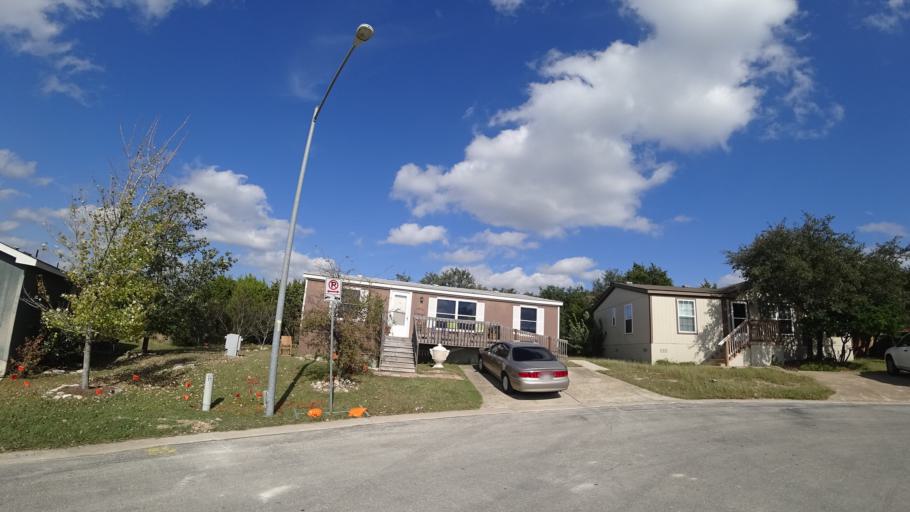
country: US
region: Texas
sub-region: Travis County
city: Barton Creek
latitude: 30.2504
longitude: -97.8819
